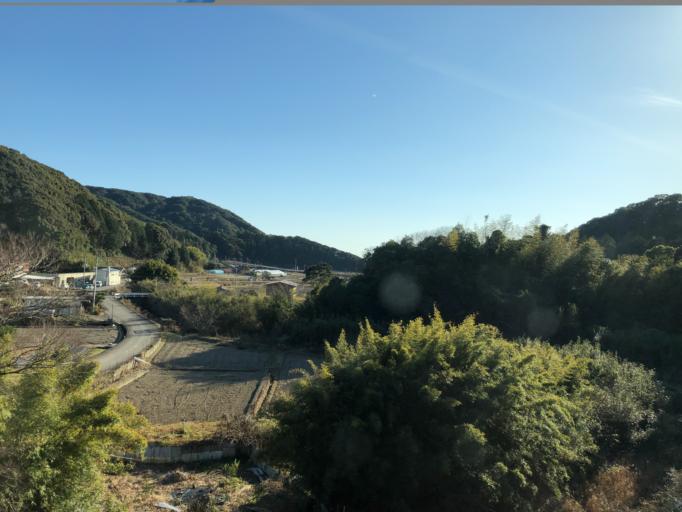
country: JP
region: Kochi
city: Nakamura
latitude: 33.0393
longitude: 133.0800
